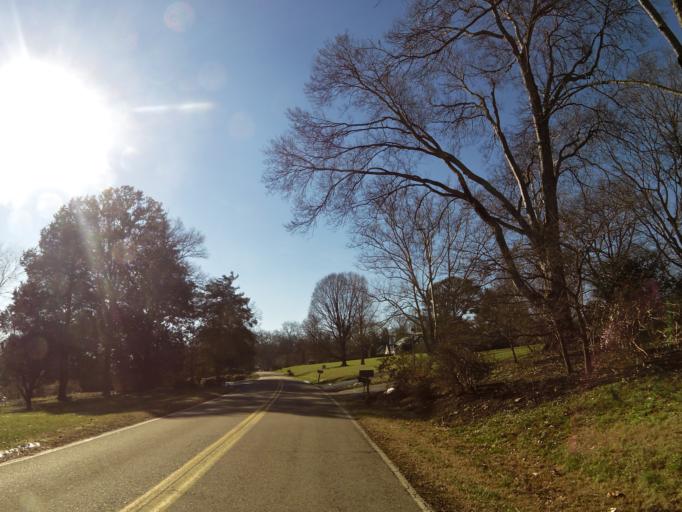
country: US
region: Tennessee
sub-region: Knox County
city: Knoxville
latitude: 35.9226
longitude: -84.0064
